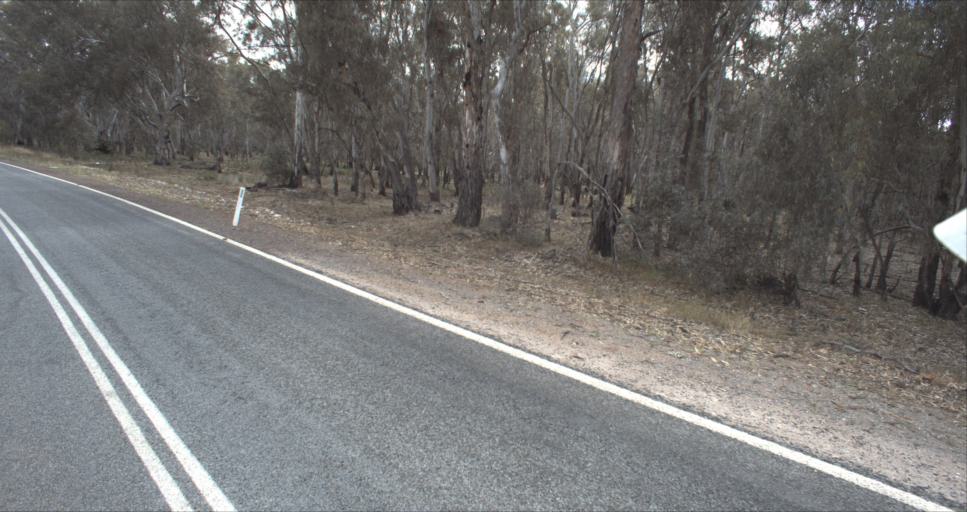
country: AU
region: New South Wales
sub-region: Leeton
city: Leeton
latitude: -34.6241
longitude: 146.3813
